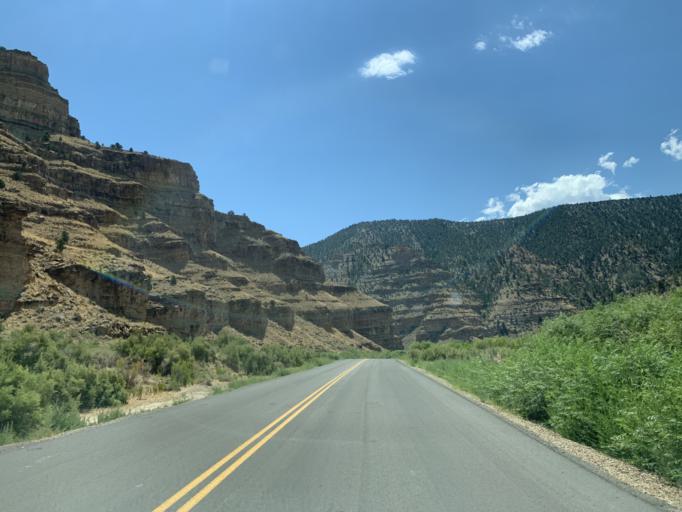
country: US
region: Utah
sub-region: Carbon County
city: East Carbon City
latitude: 39.8120
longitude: -110.2736
